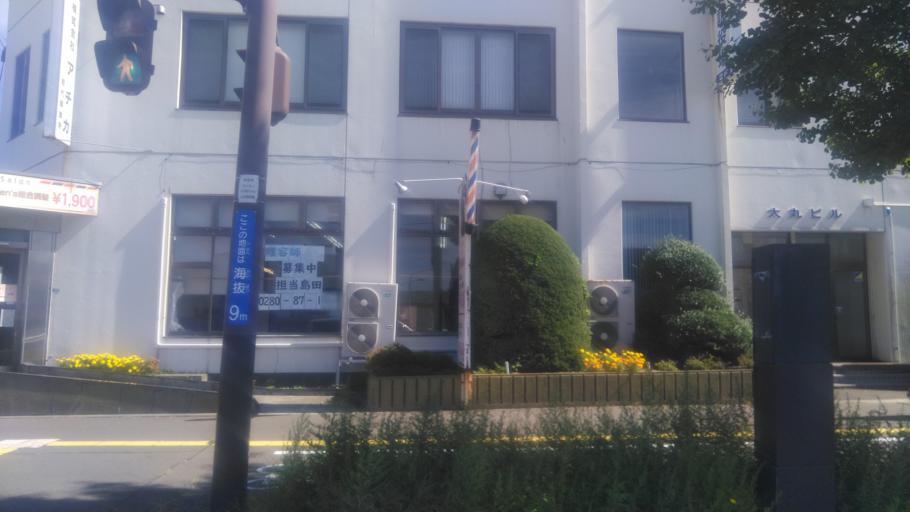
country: JP
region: Akita
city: Noshiromachi
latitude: 40.2039
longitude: 140.0225
